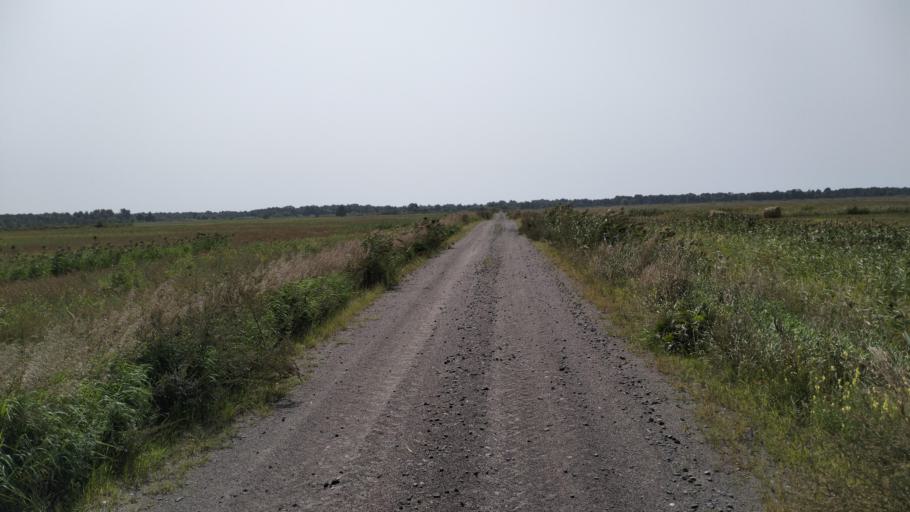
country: BY
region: Brest
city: Davyd-Haradok
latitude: 51.9776
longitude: 27.1746
